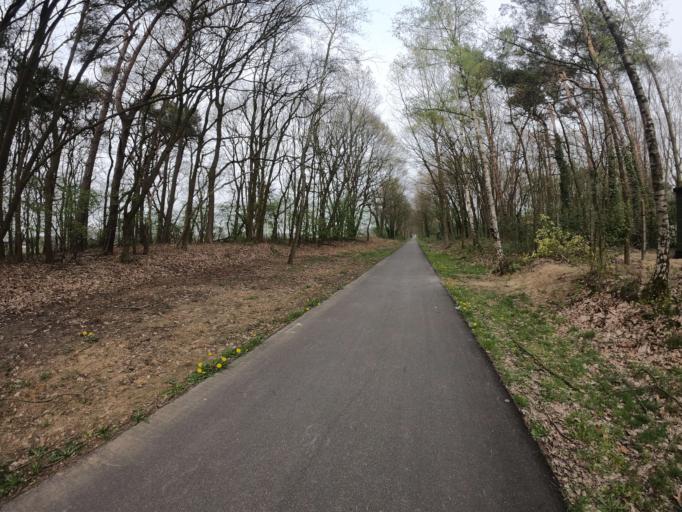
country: BE
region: Flanders
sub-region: Provincie Limburg
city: Maaseik
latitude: 51.0877
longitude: 5.7607
